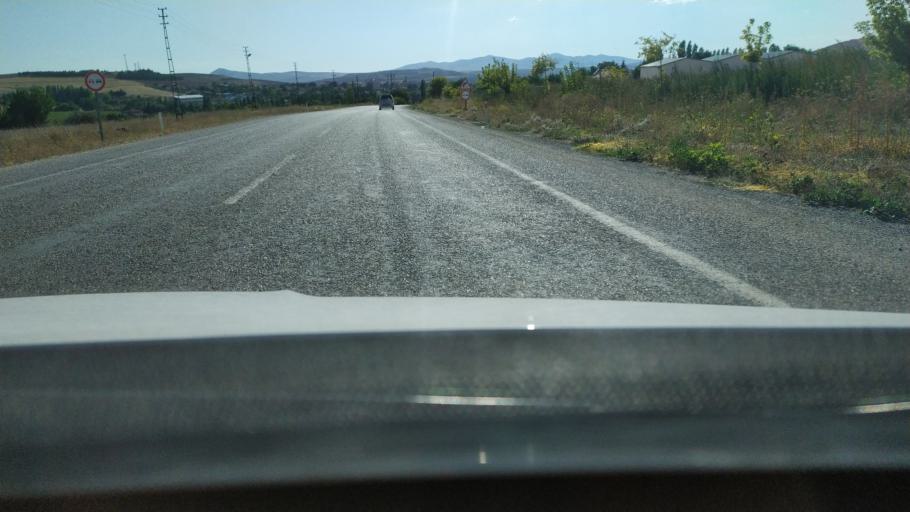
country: TR
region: Kayseri
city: Felahiye
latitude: 39.0972
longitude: 35.5821
